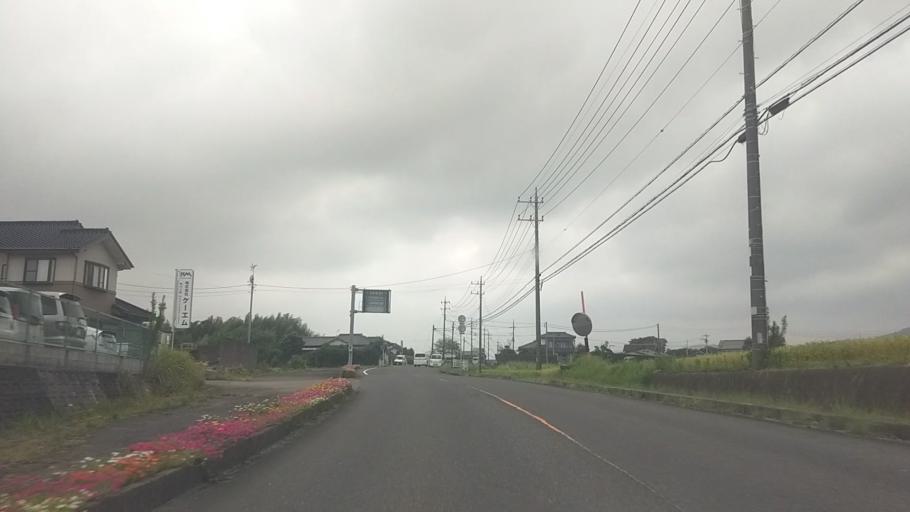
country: JP
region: Chiba
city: Kawaguchi
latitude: 35.1154
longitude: 140.0792
